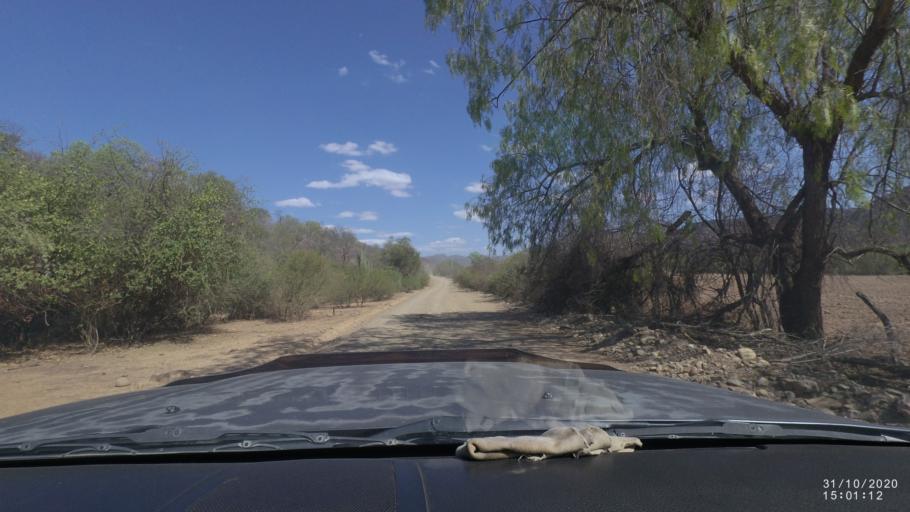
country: BO
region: Cochabamba
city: Aiquile
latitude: -18.2621
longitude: -64.8205
